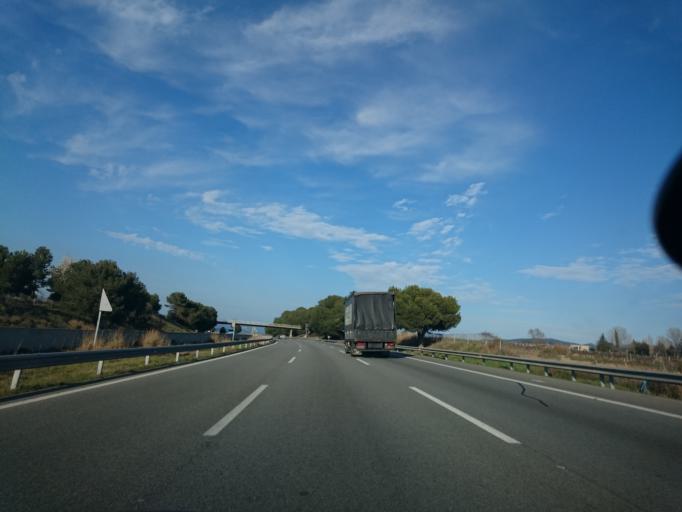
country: ES
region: Catalonia
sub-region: Provincia de Barcelona
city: La Granada
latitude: 41.3732
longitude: 1.7330
